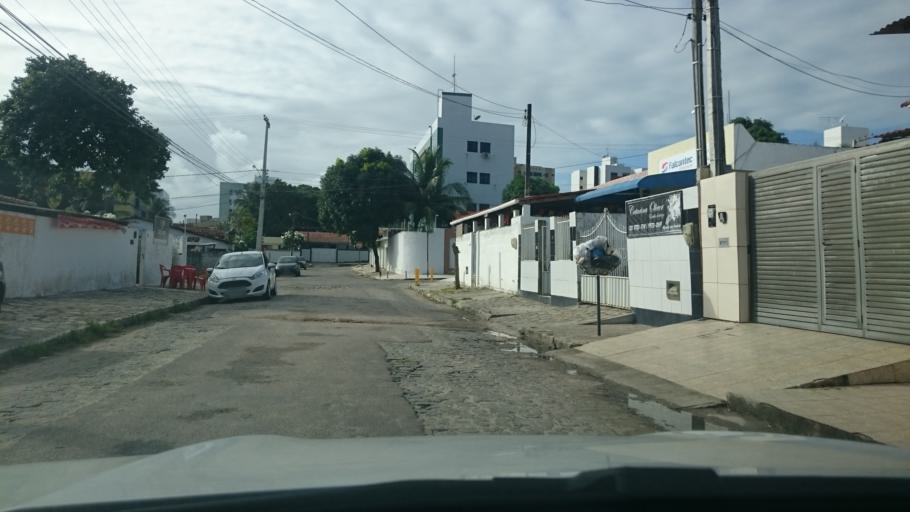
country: BR
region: Paraiba
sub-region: Joao Pessoa
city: Joao Pessoa
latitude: -7.1539
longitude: -34.8429
